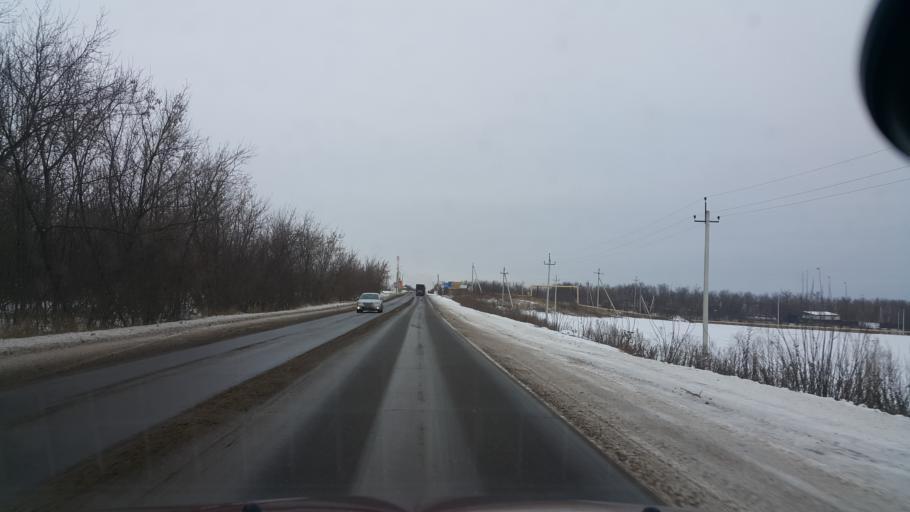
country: RU
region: Tambov
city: Pokrovo-Prigorodnoye
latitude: 52.6589
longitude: 41.4065
